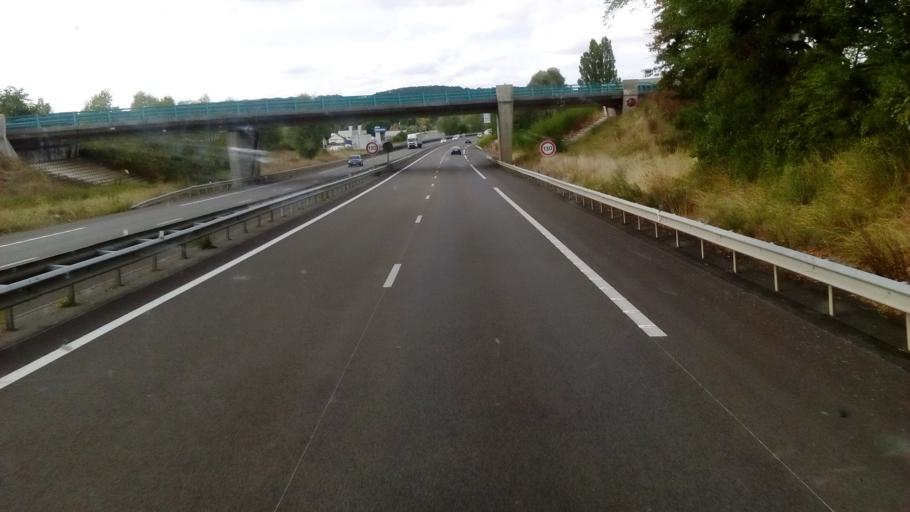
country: FR
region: Bourgogne
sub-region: Departement de la Nievre
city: Varennes-Vauzelles
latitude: 47.0432
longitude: 3.1369
